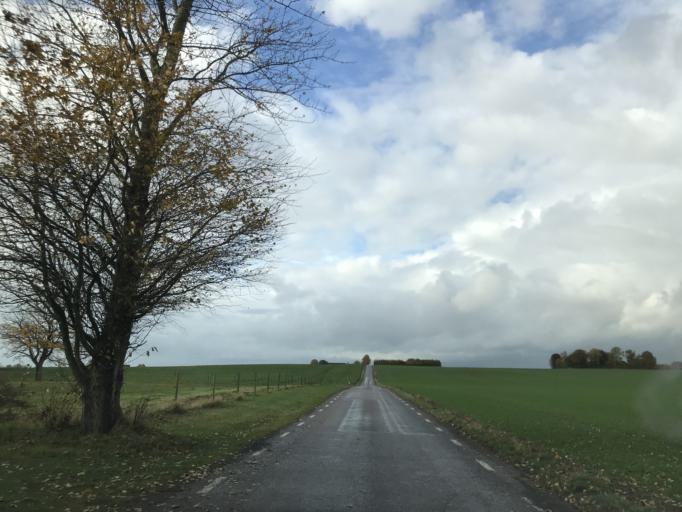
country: SE
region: Skane
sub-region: Svalovs Kommun
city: Svaloev
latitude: 55.9040
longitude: 13.1775
